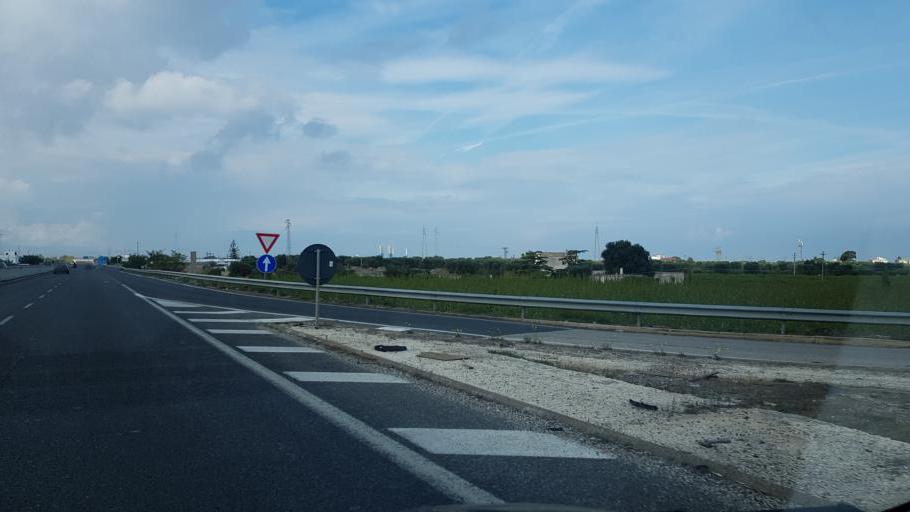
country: IT
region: Apulia
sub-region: Provincia di Bari
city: Monopoli
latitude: 40.9420
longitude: 17.2804
